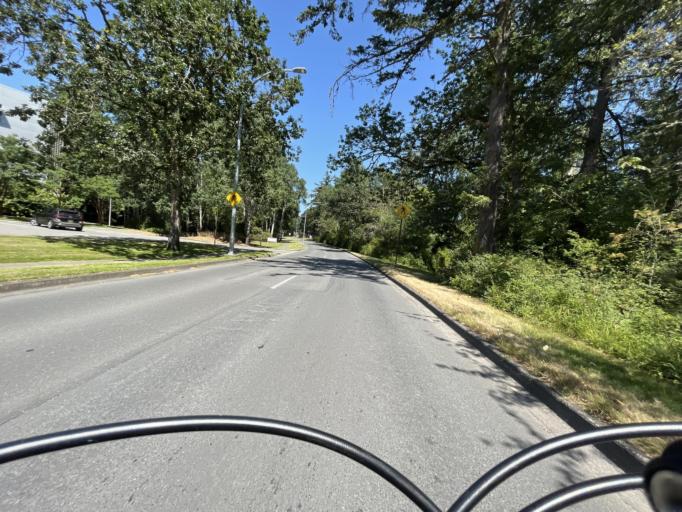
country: CA
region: British Columbia
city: Oak Bay
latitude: 48.4606
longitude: -123.3102
